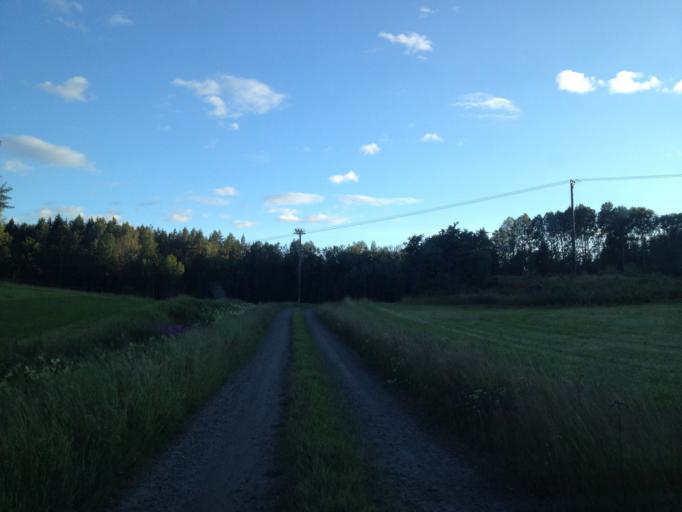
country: SE
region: Kalmar
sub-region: Vasterviks Kommun
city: Overum
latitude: 57.9930
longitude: 16.1769
